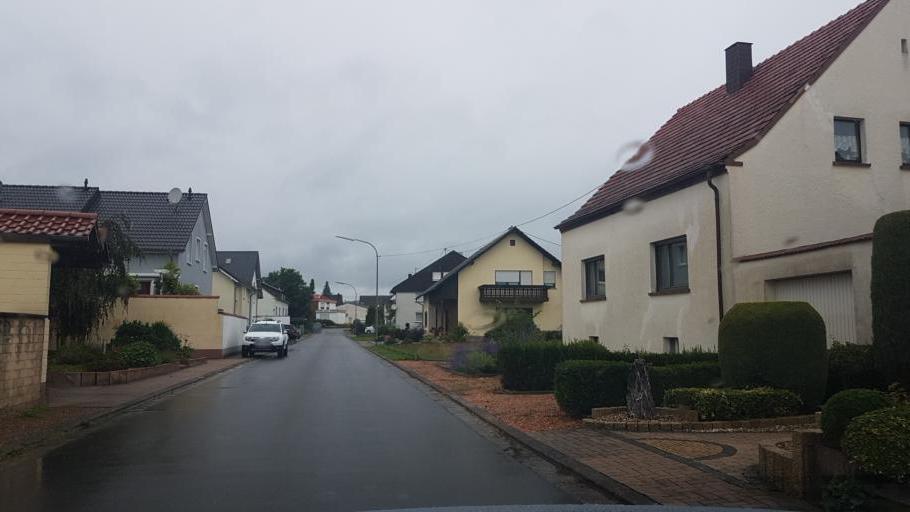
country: DE
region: Saarland
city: Losheim
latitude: 49.5113
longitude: 6.7515
